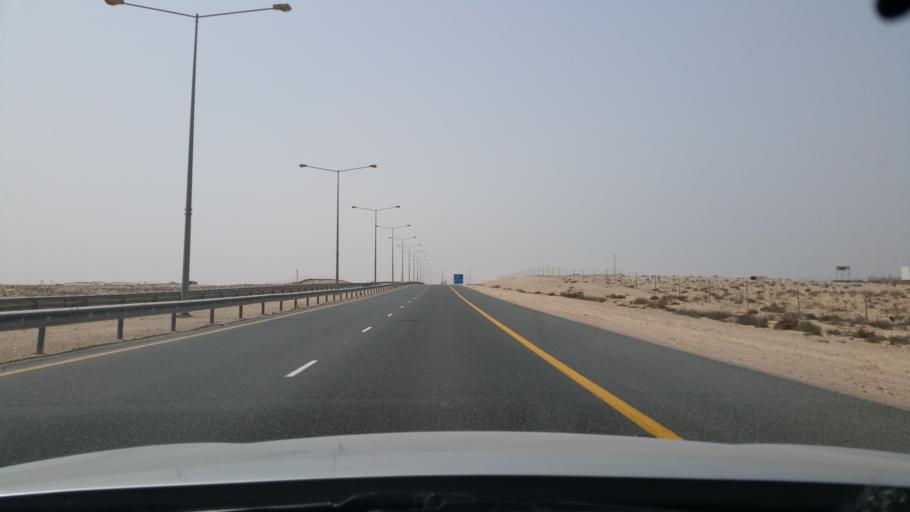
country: QA
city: Umm Bab
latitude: 25.3060
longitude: 50.7922
